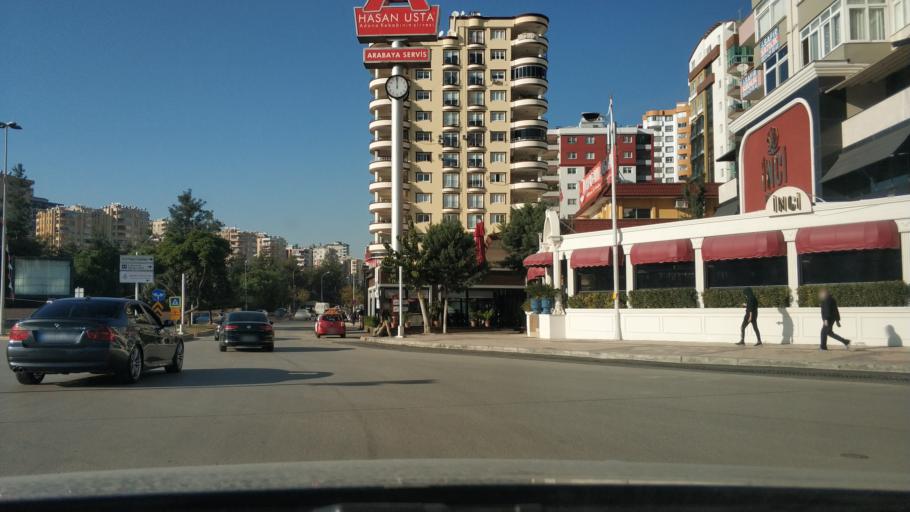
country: TR
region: Adana
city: Seyhan
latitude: 37.0487
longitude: 35.2809
